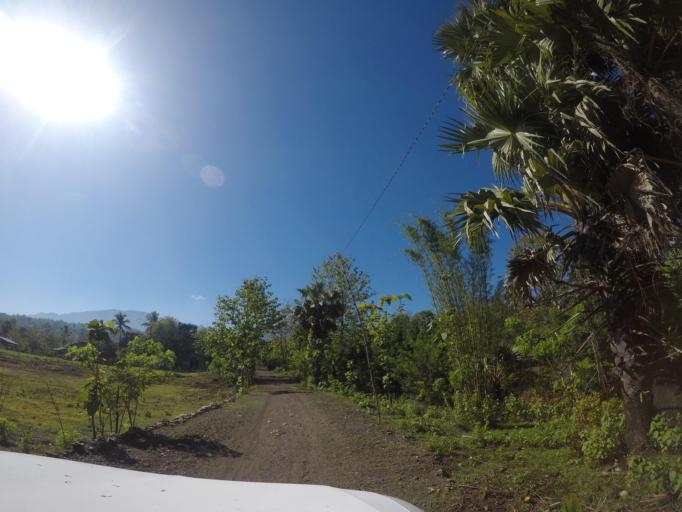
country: TL
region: Bobonaro
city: Maliana
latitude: -8.9955
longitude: 125.2042
